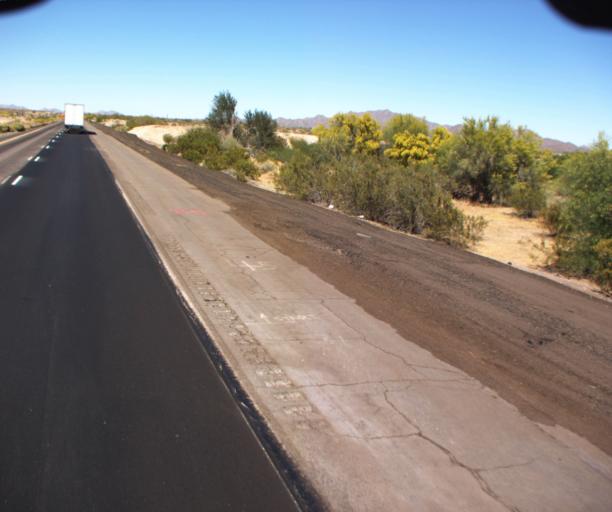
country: US
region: Arizona
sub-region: Maricopa County
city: Gila Bend
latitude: 33.0755
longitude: -112.6463
